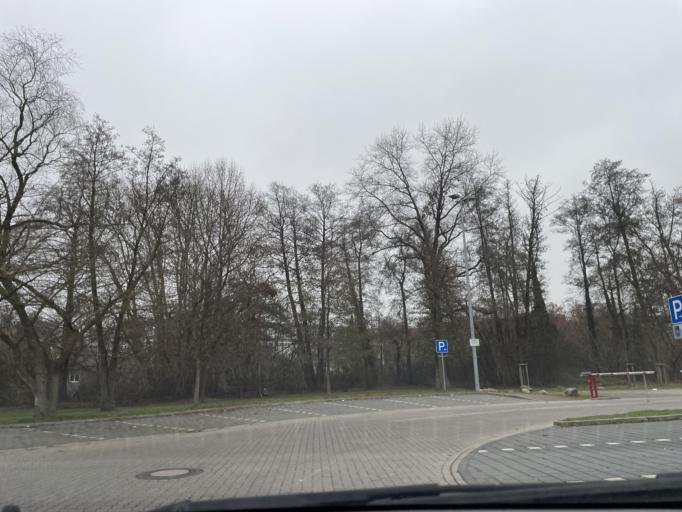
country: DE
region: Lower Saxony
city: Uelzen
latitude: 52.9607
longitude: 10.5585
